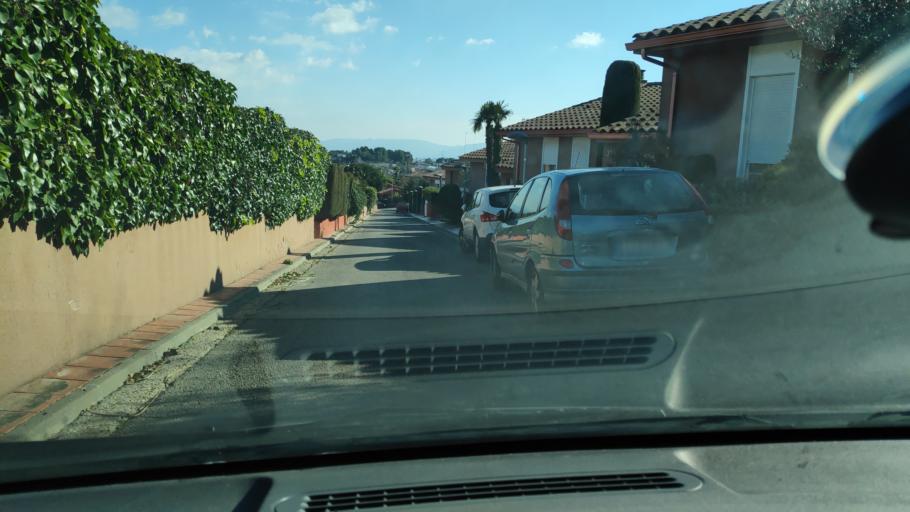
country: ES
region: Catalonia
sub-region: Provincia de Barcelona
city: Sant Quirze del Valles
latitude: 41.5250
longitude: 2.0690
